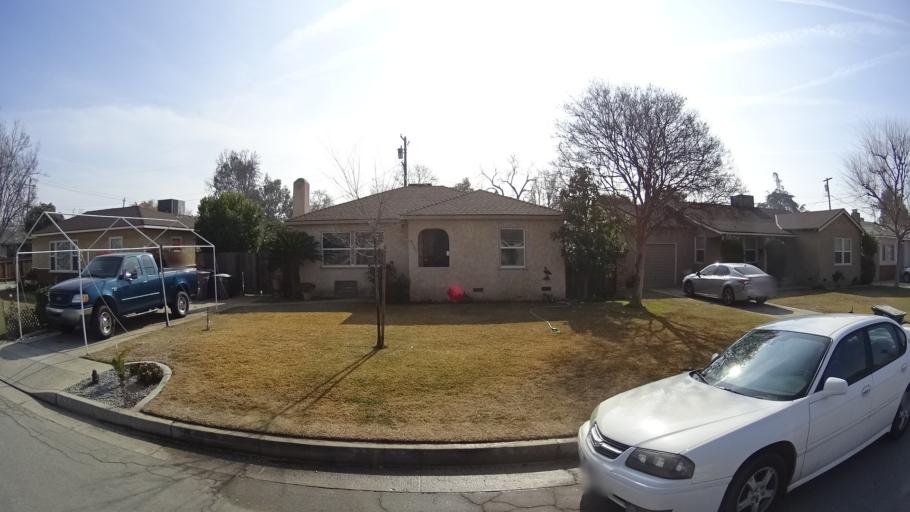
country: US
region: California
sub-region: Kern County
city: Bakersfield
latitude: 35.3606
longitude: -119.0325
